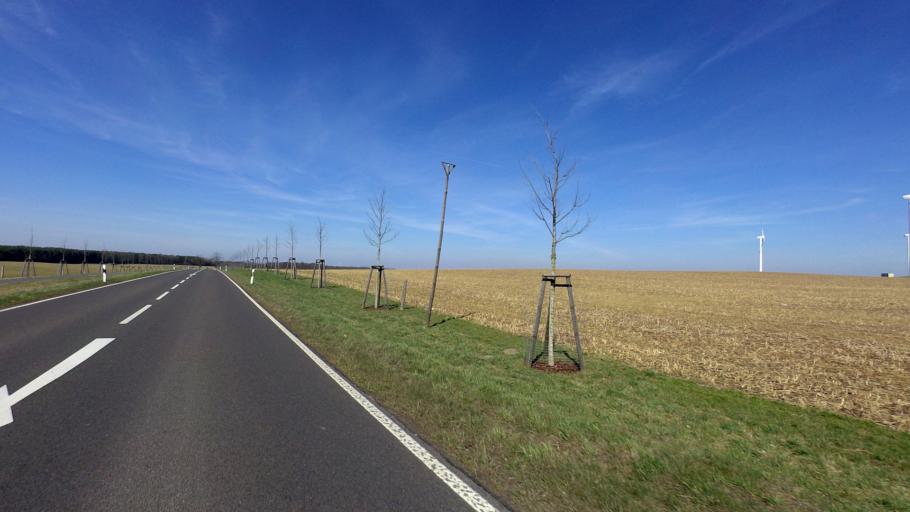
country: DE
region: Brandenburg
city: Furstenwalde
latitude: 52.3883
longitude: 14.0500
